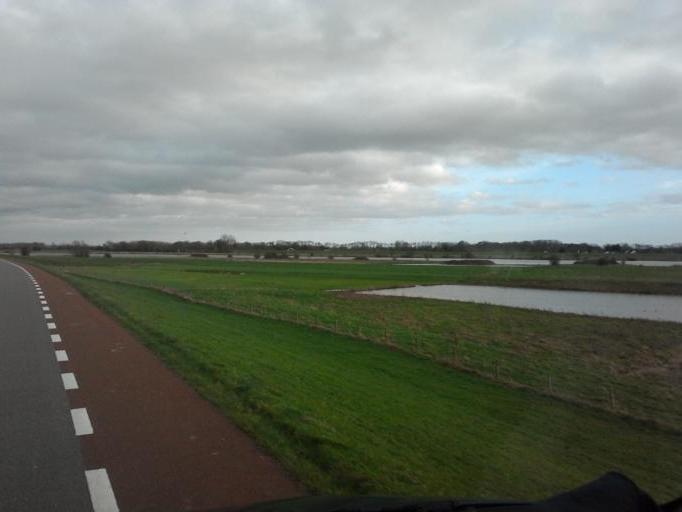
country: NL
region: Gelderland
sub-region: Gemeente Culemborg
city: Culemborg
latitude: 51.9680
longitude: 5.2163
